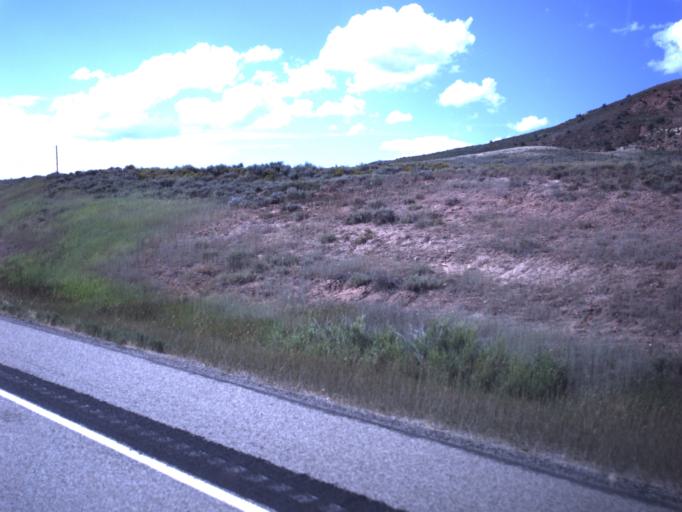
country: US
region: Utah
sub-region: Wasatch County
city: Heber
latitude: 40.1961
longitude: -111.0950
